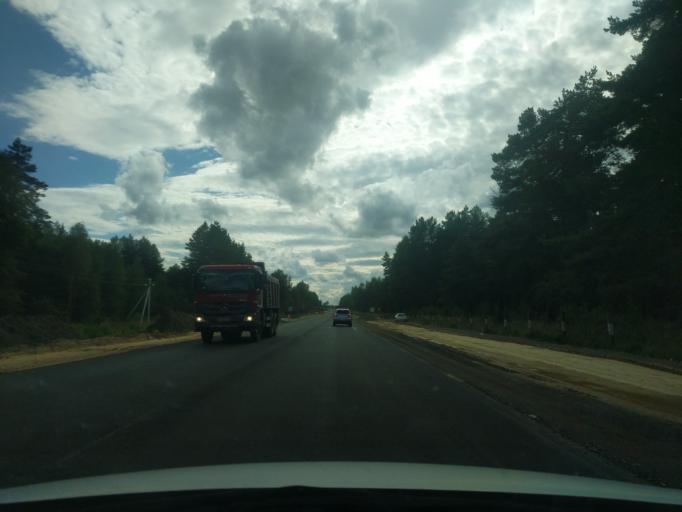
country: RU
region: Jaroslavl
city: Levashevo
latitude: 57.6684
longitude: 40.5771
